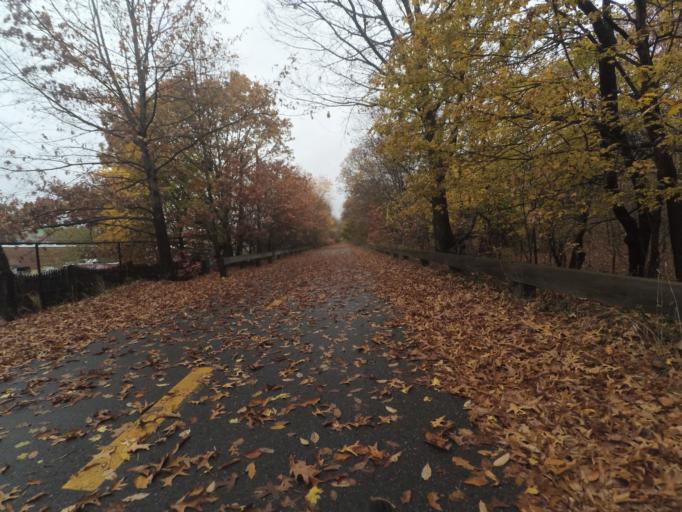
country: US
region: Massachusetts
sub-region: Middlesex County
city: Arlington
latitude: 42.4234
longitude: -71.1705
